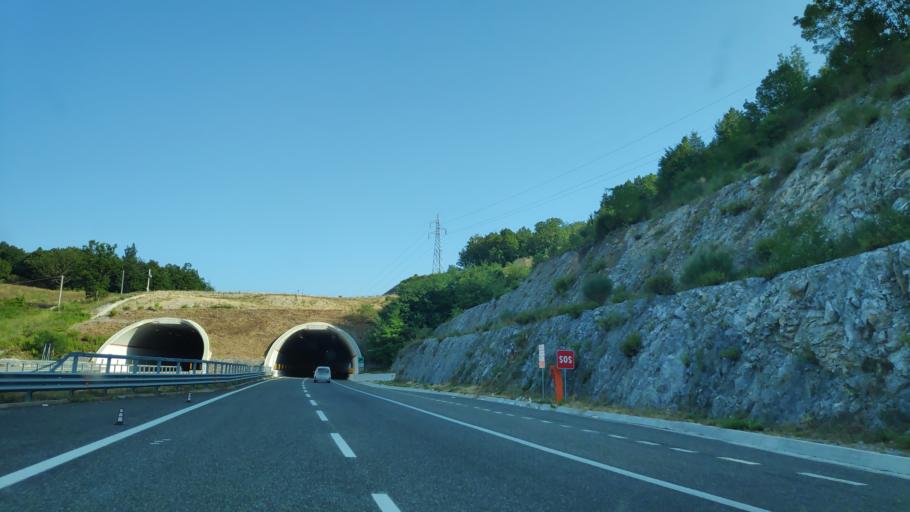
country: IT
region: Basilicate
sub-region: Provincia di Potenza
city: Lauria
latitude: 40.0280
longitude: 15.8760
